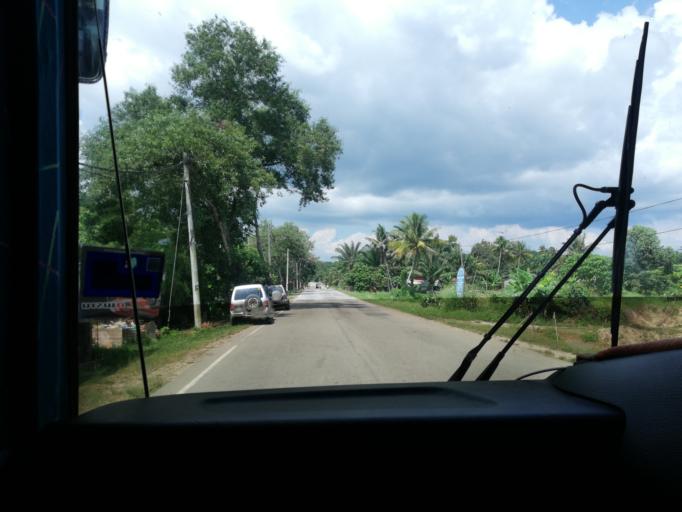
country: MY
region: Perak
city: Parit Buntar
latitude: 5.1190
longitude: 100.5628
